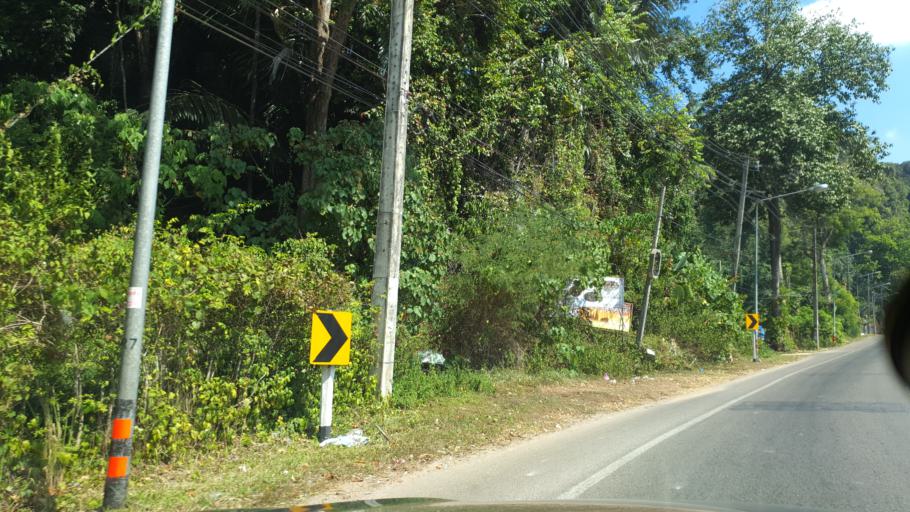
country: TH
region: Krabi
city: Krabi
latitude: 8.0852
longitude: 98.8740
